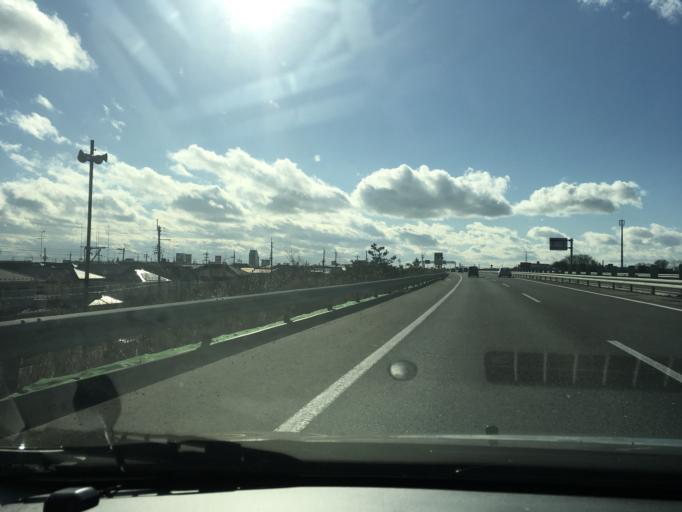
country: JP
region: Miyagi
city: Ishinomaki
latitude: 38.4543
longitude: 141.2734
